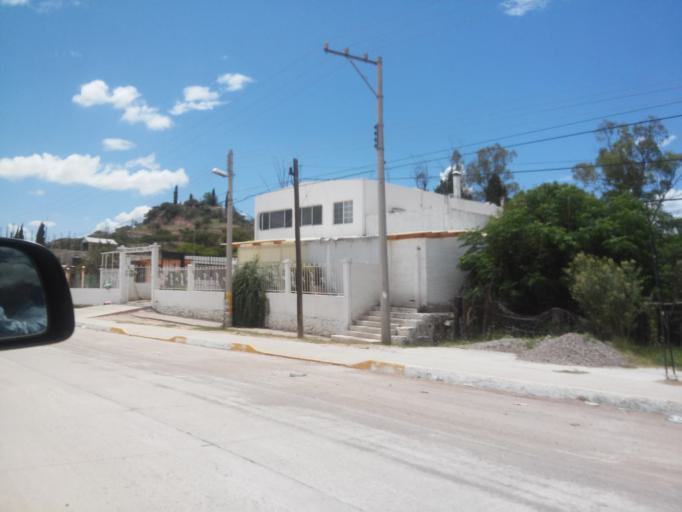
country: MX
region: Durango
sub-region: Santiago Papasquiaro
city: Santiago Papasquiaro
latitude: 25.0577
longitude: -105.4256
